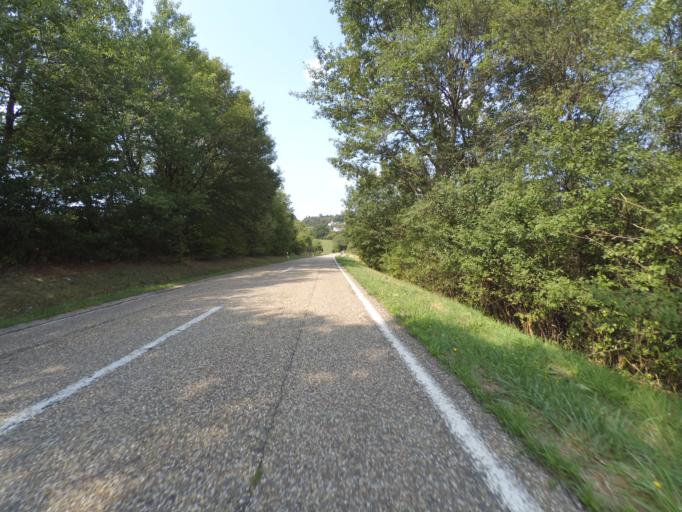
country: DE
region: Saarland
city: Britten
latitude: 49.5166
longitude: 6.6838
